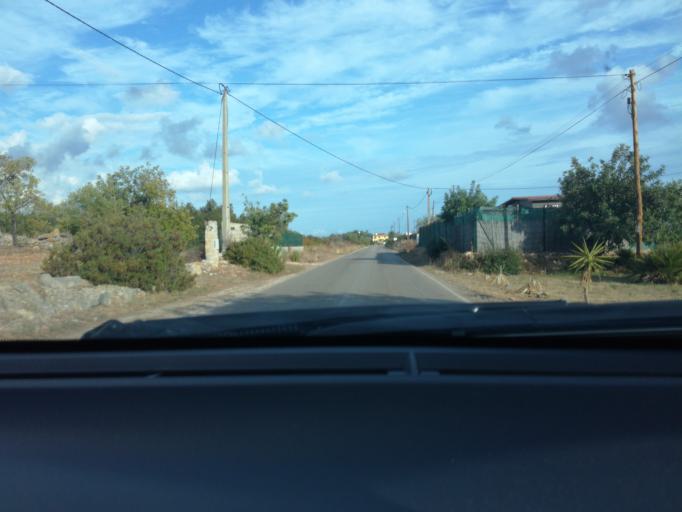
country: PT
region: Faro
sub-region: Olhao
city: Laranjeiro
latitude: 37.0781
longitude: -7.8235
